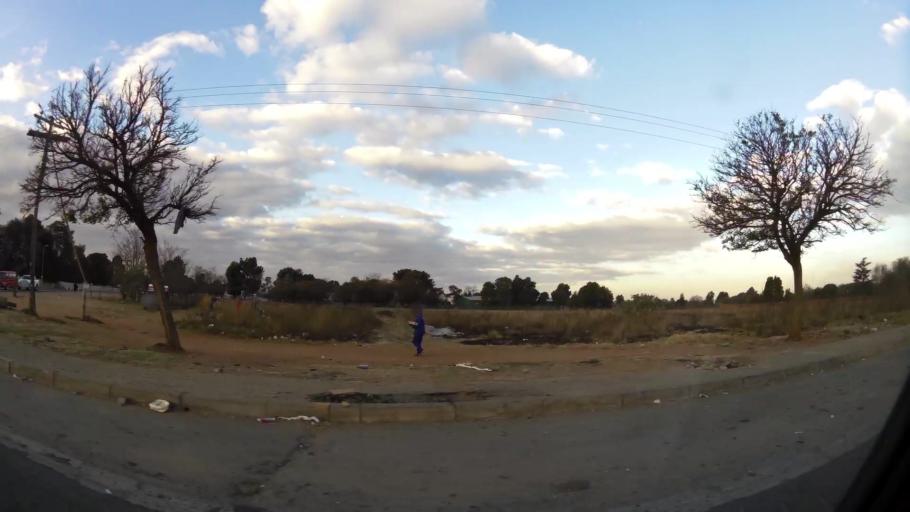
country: ZA
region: Gauteng
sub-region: City of Johannesburg Metropolitan Municipality
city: Midrand
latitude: -25.9895
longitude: 28.1532
